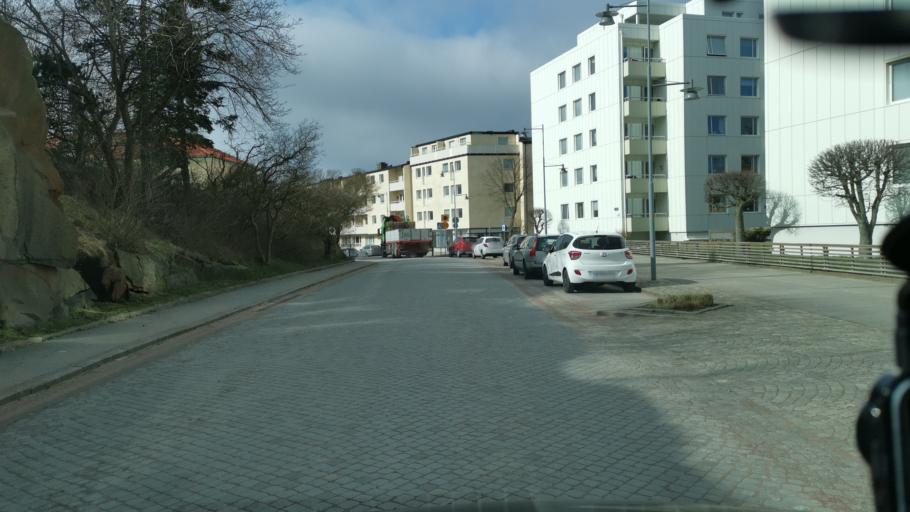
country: SE
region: Vaestra Goetaland
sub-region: Lysekils Kommun
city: Lysekil
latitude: 58.2738
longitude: 11.4325
